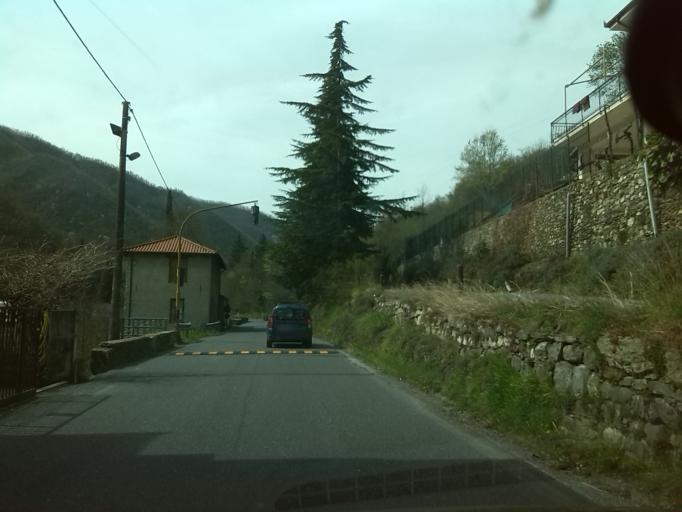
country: IT
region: Liguria
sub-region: Provincia di Imperia
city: Borghetto d'Arroscia
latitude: 44.0563
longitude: 7.9801
